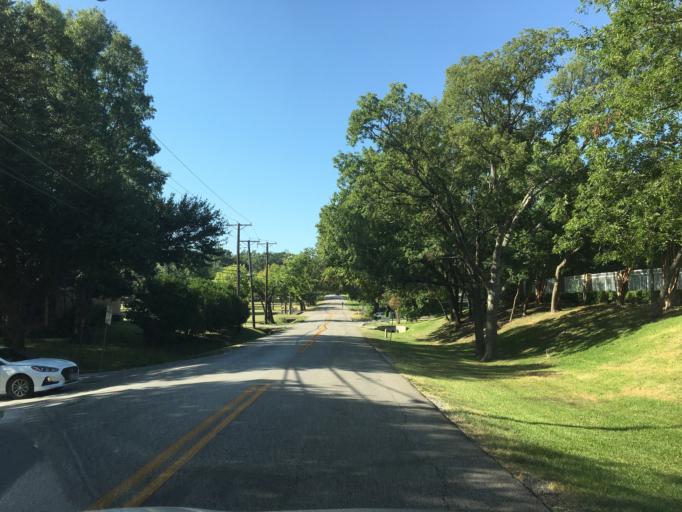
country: US
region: Texas
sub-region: Dallas County
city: Highland Park
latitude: 32.8730
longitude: -96.7288
